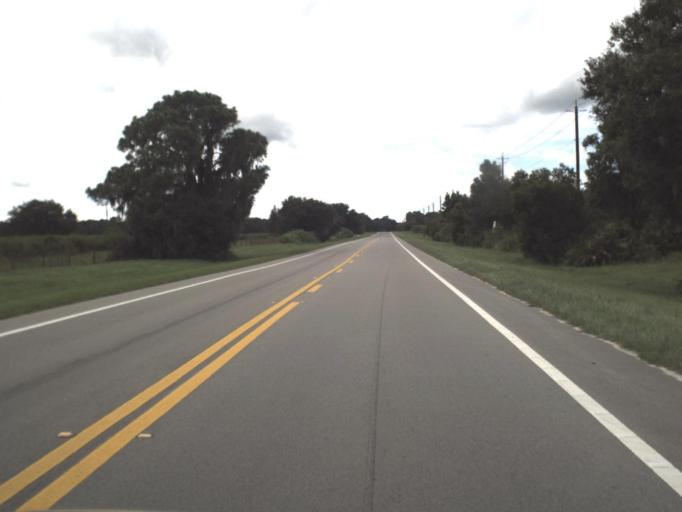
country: US
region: Florida
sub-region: Hillsborough County
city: Ruskin
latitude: 27.5869
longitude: -82.3986
